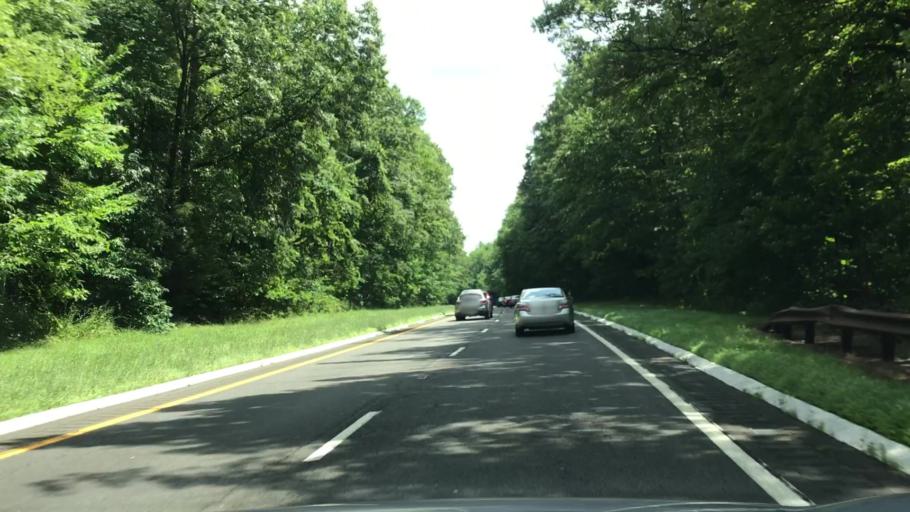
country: US
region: New York
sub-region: Rockland County
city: New Square
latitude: 41.1279
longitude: -74.0149
